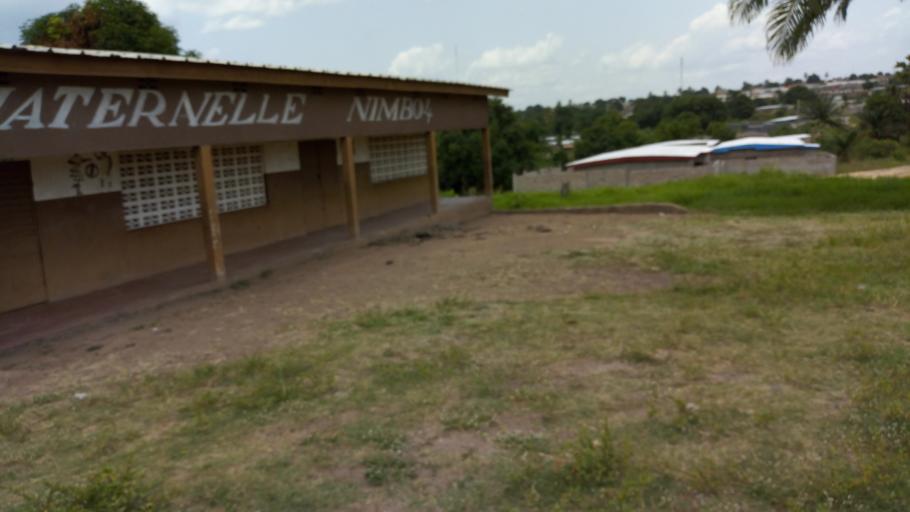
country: CI
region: Vallee du Bandama
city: Bouake
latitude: 7.6674
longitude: -5.0258
